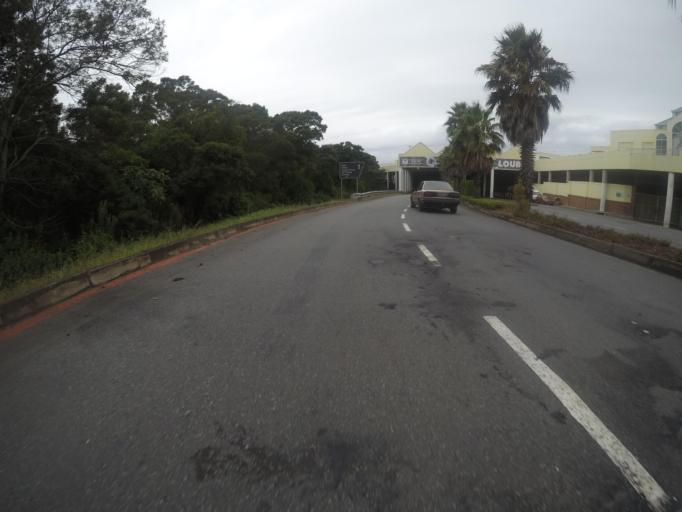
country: ZA
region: Eastern Cape
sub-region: Buffalo City Metropolitan Municipality
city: East London
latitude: -32.9695
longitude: 27.8982
